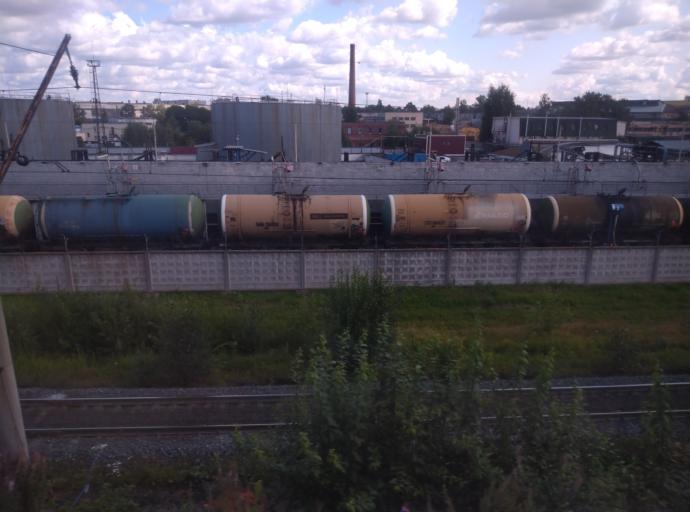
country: RU
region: St.-Petersburg
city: Centralniy
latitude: 59.9017
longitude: 30.3821
